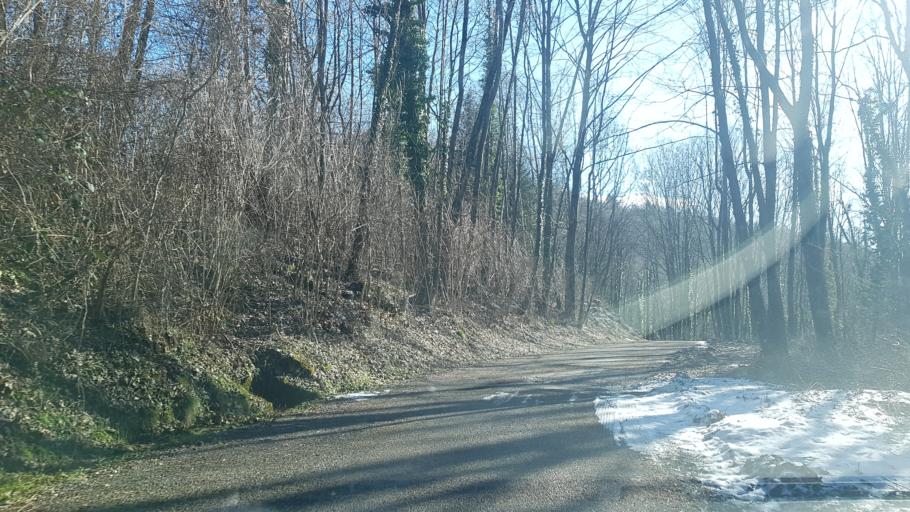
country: IT
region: Friuli Venezia Giulia
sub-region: Provincia di Udine
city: Tarcento
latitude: 46.2553
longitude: 13.2282
